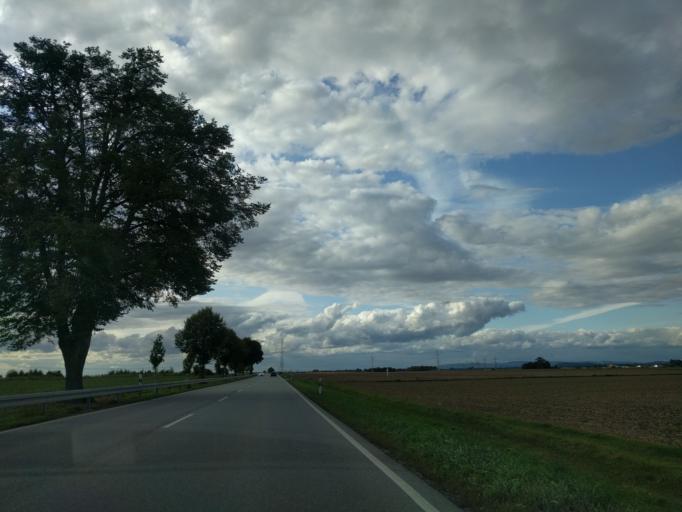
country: DE
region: Bavaria
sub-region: Lower Bavaria
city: Stephansposching
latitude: 48.8097
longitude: 12.7765
